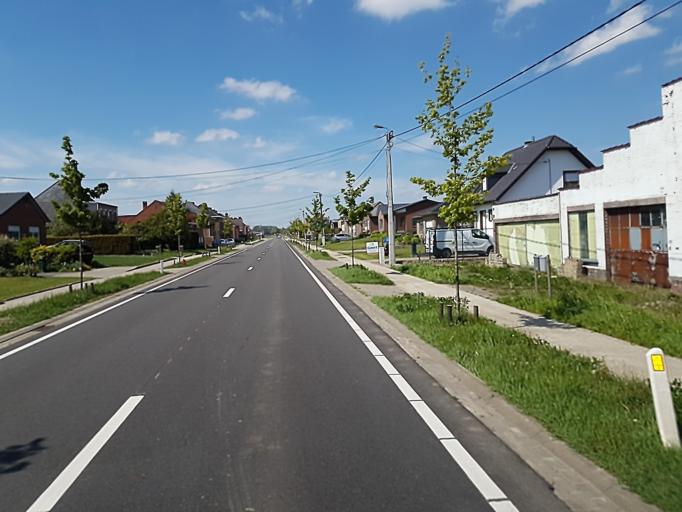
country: BE
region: Flanders
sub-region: Provincie Vlaams-Brabant
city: Glabbeek-Zuurbemde
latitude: 50.8563
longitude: 4.8993
